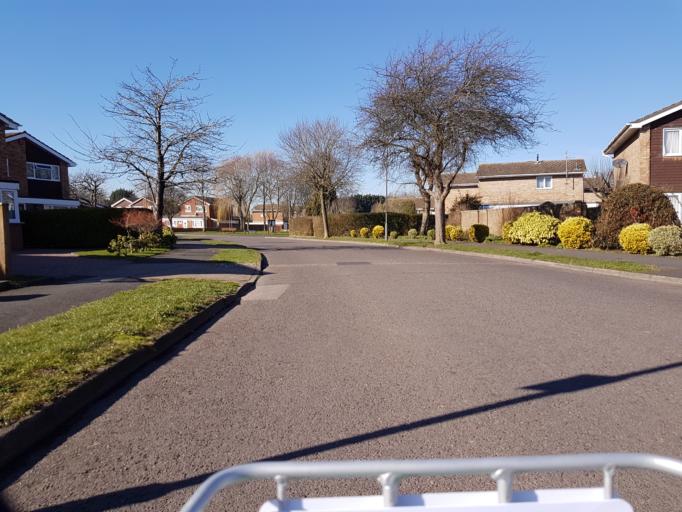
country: GB
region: England
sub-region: Buckinghamshire
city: Newton Longville
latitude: 51.9923
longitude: -0.7651
